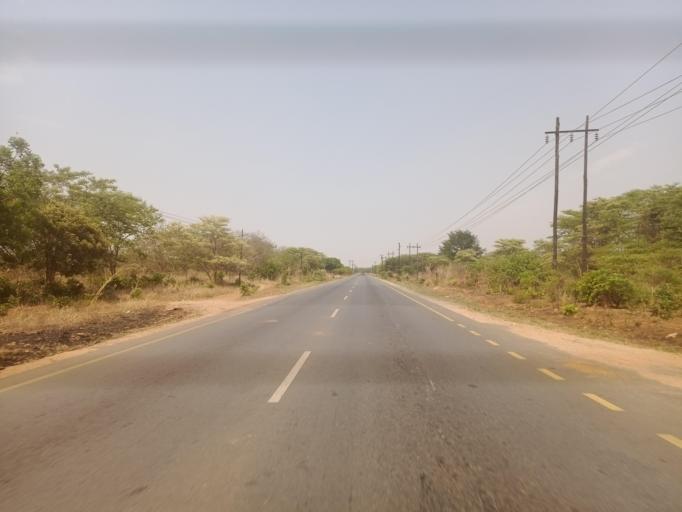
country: ZM
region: Lusaka
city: Lusaka
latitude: -15.2787
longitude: 28.3989
